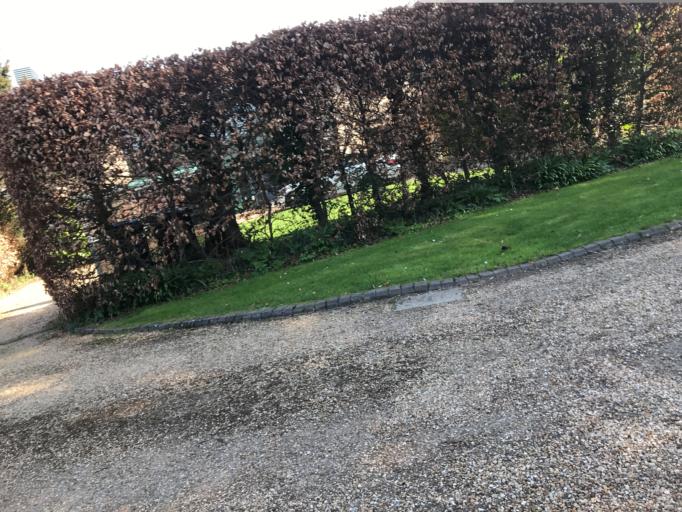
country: GB
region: England
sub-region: Cambridgeshire
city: Sawston
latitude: 52.1561
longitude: 0.1445
